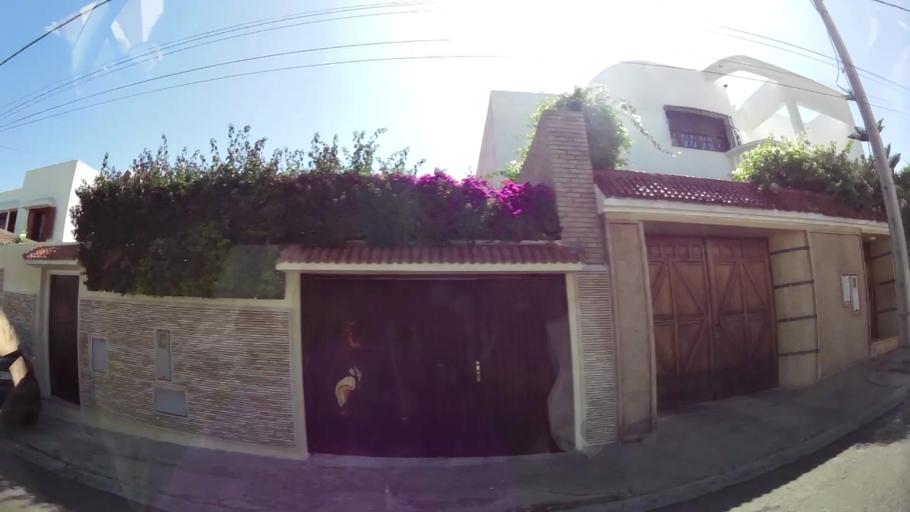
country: MA
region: Souss-Massa-Draa
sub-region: Agadir-Ida-ou-Tnan
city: Agadir
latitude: 30.4263
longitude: -9.6019
